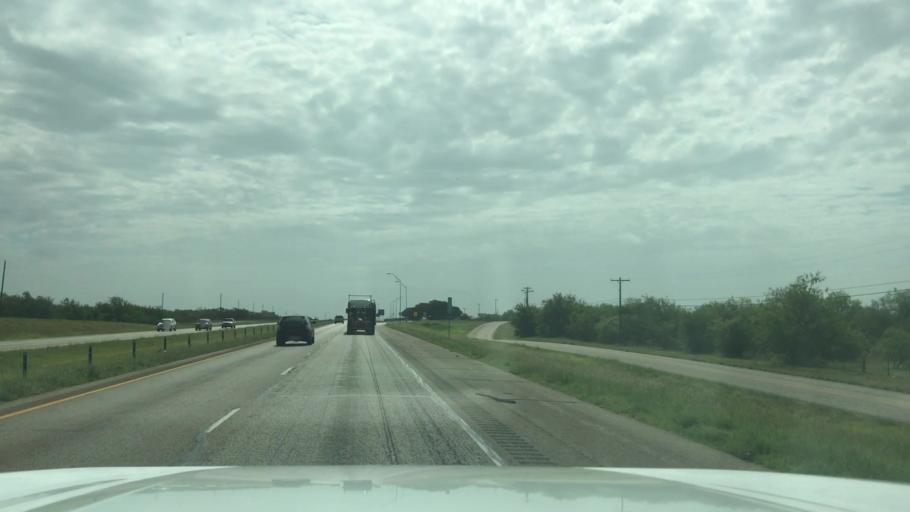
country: US
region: Texas
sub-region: Callahan County
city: Clyde
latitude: 32.4288
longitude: -99.5866
